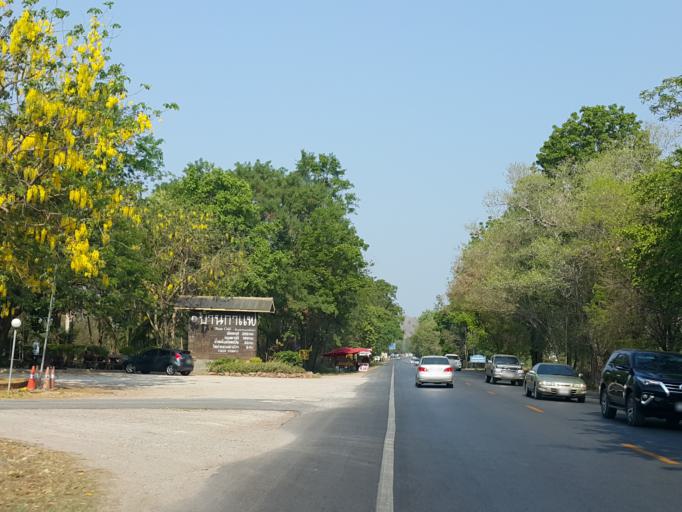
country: TH
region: Kanchanaburi
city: Sai Yok
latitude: 14.0898
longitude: 99.2885
